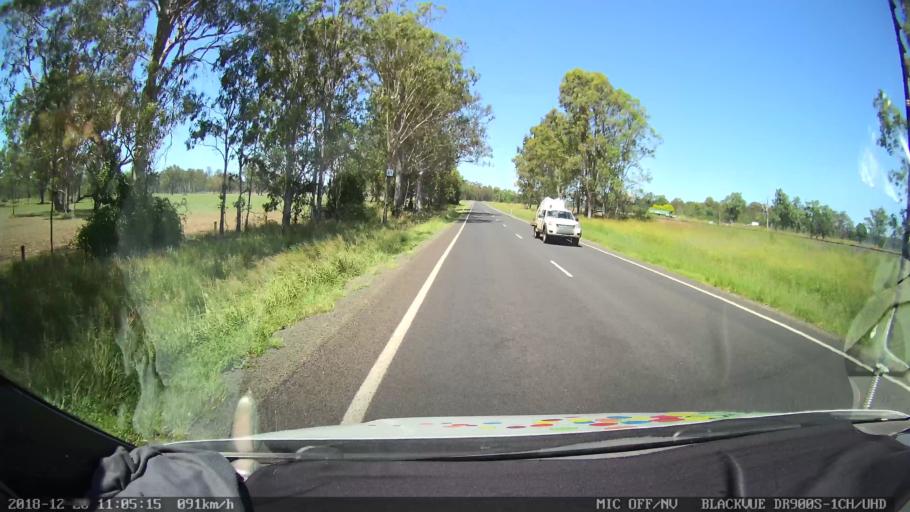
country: AU
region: New South Wales
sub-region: Richmond Valley
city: Casino
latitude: -28.8941
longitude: 153.0419
